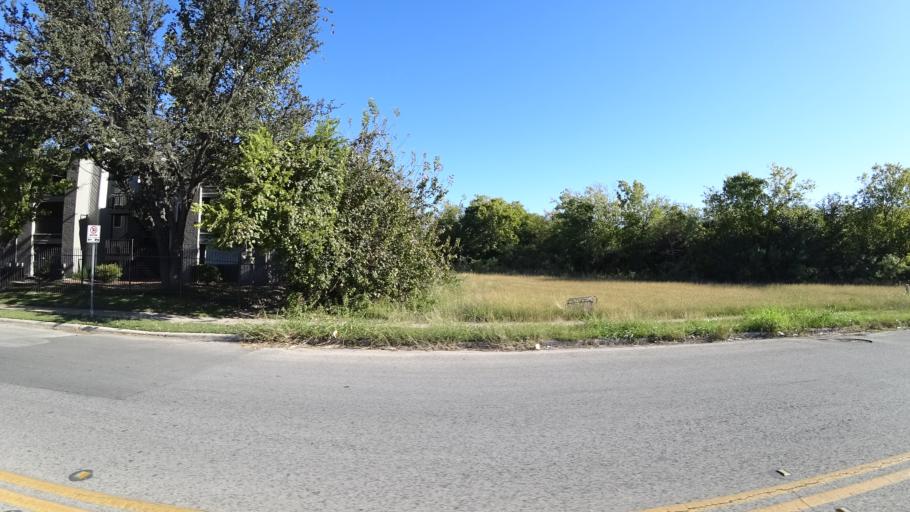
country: US
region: Texas
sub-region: Travis County
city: Austin
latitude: 30.3042
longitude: -97.6630
